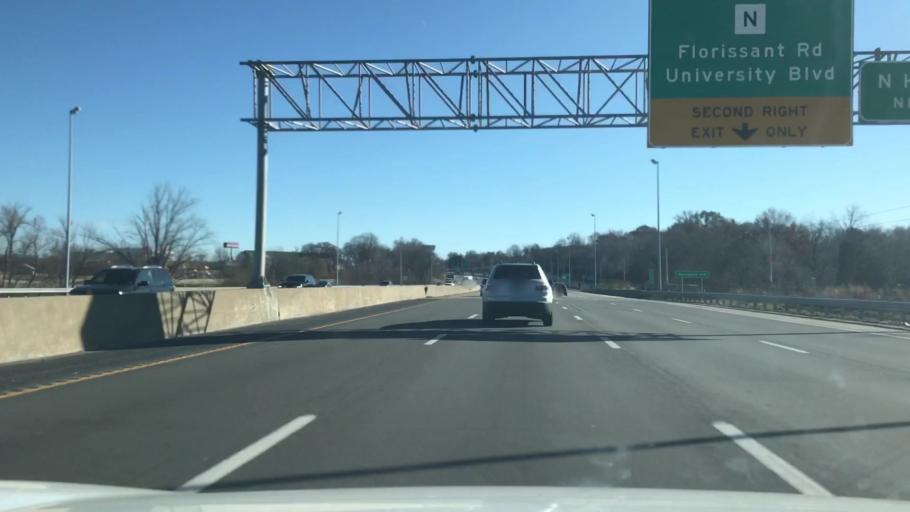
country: US
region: Missouri
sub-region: Saint Louis County
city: Bel-Ridge
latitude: 38.7252
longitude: -90.3258
